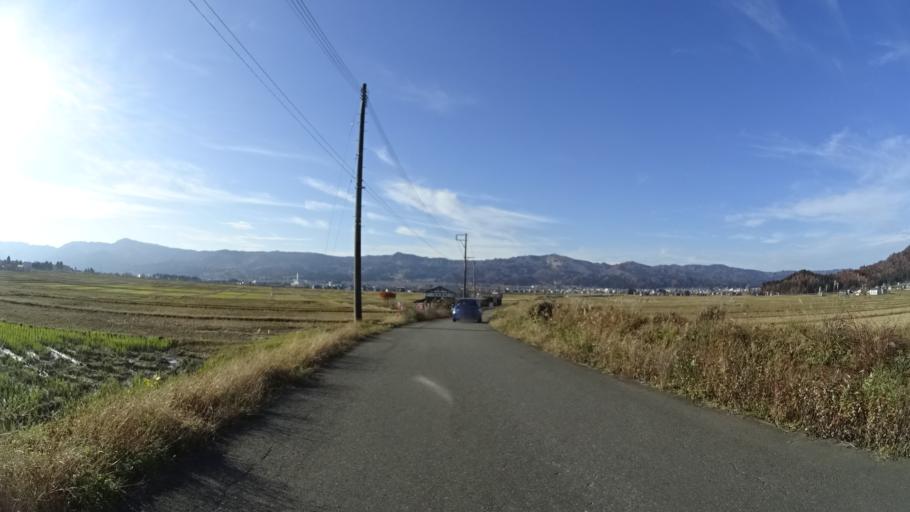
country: JP
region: Niigata
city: Muikamachi
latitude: 37.0355
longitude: 138.8879
